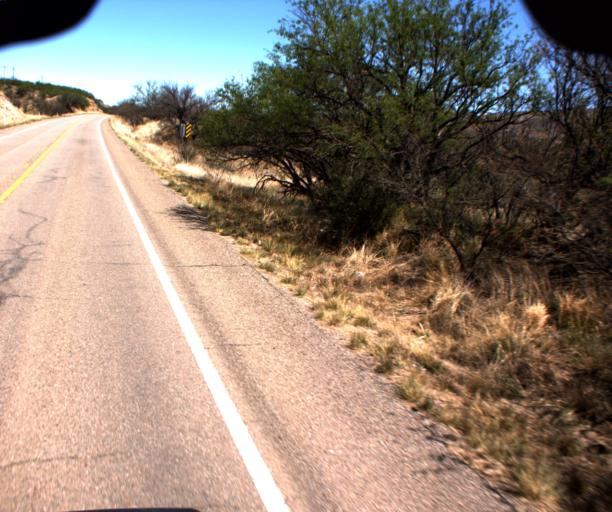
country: US
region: Arizona
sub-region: Santa Cruz County
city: Rio Rico
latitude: 31.5882
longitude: -110.7267
